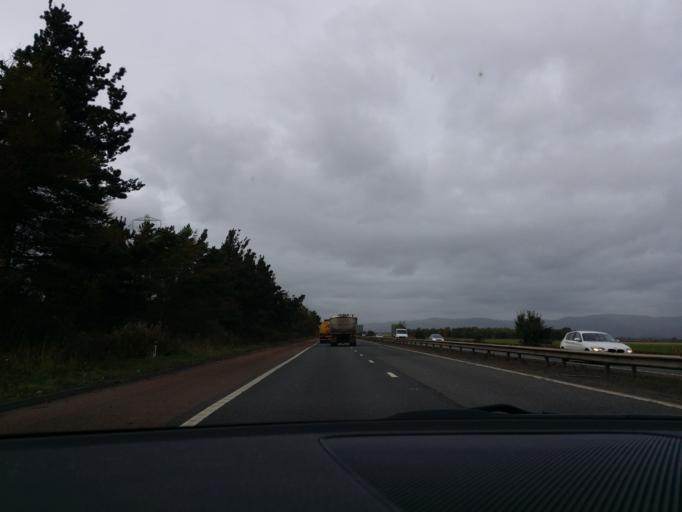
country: GB
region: Scotland
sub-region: Falkirk
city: Airth
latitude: 56.0303
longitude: -3.7642
